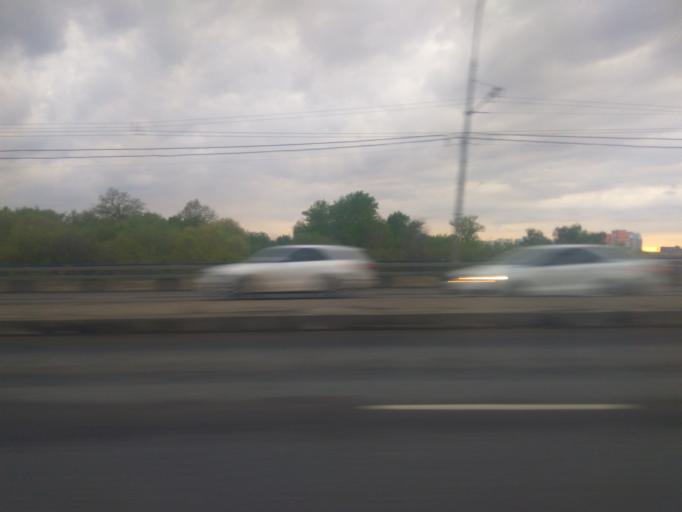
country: RU
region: Moskovskaya
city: Novogireyevo
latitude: 55.7421
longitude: 37.8159
